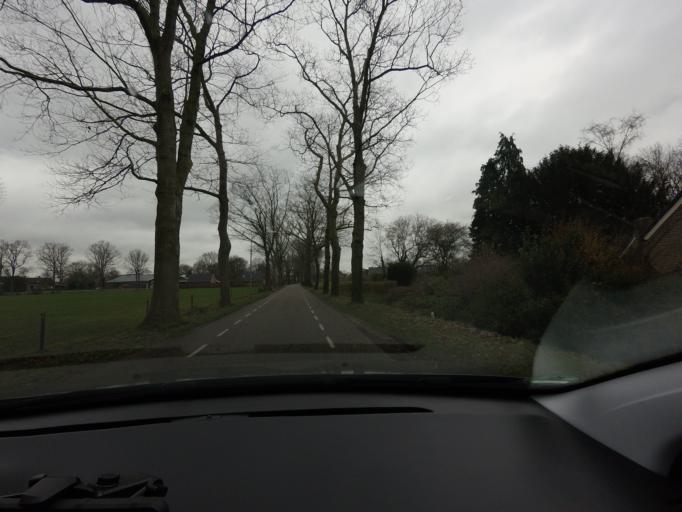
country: NL
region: Drenthe
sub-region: Gemeente Hoogeveen
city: Hoogeveen
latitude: 52.8126
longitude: 6.5165
